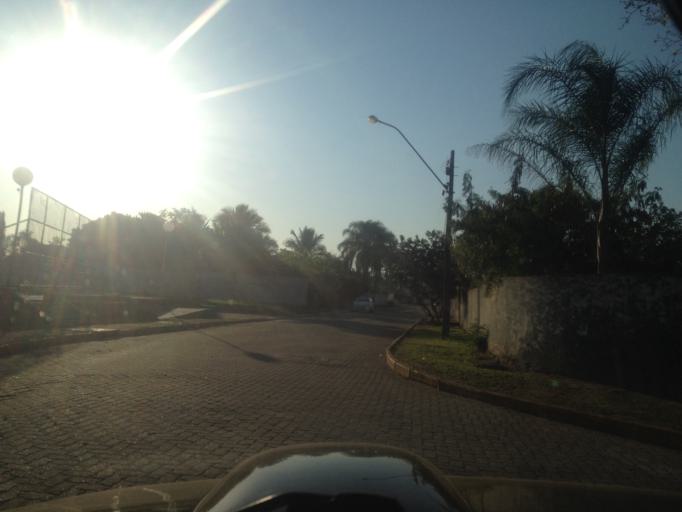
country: BR
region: Rio de Janeiro
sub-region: Porto Real
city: Porto Real
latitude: -22.4209
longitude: -44.2942
